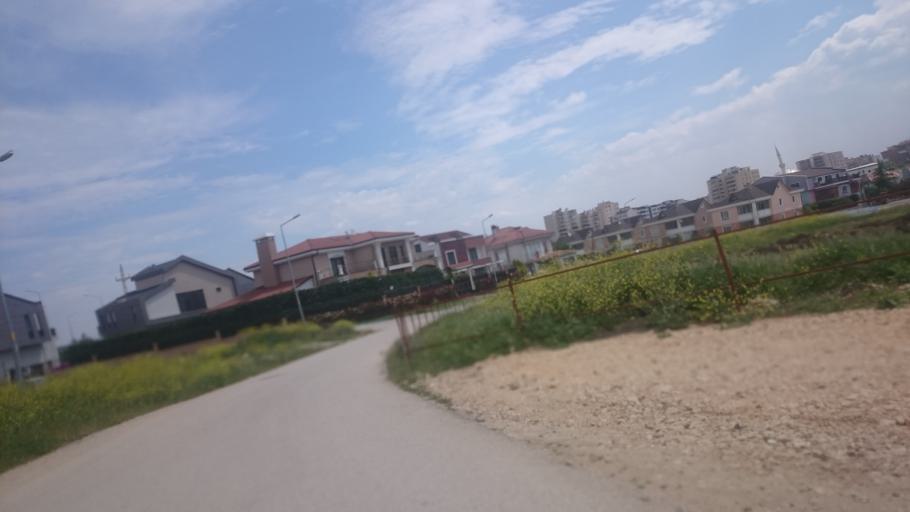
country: TR
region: Bursa
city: Gorukle
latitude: 40.2275
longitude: 28.9010
